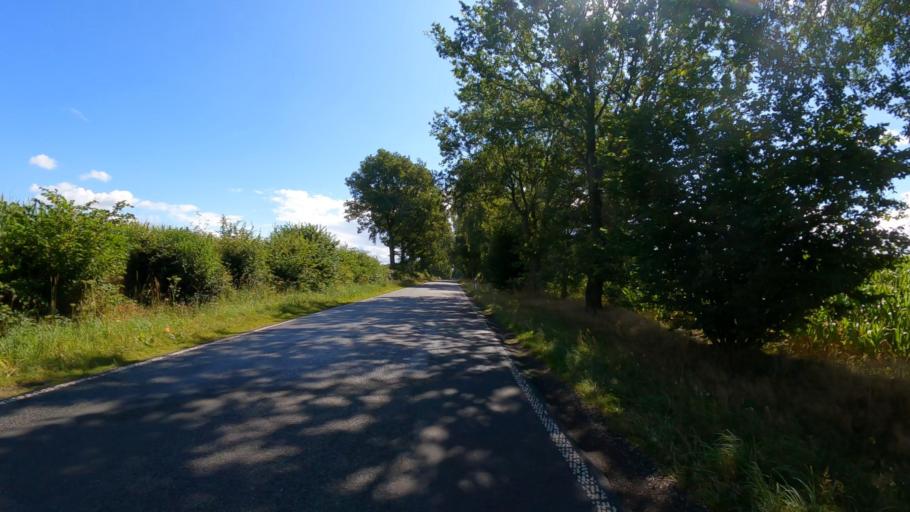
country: DE
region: Schleswig-Holstein
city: Armstedt
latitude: 53.9604
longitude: 9.8609
